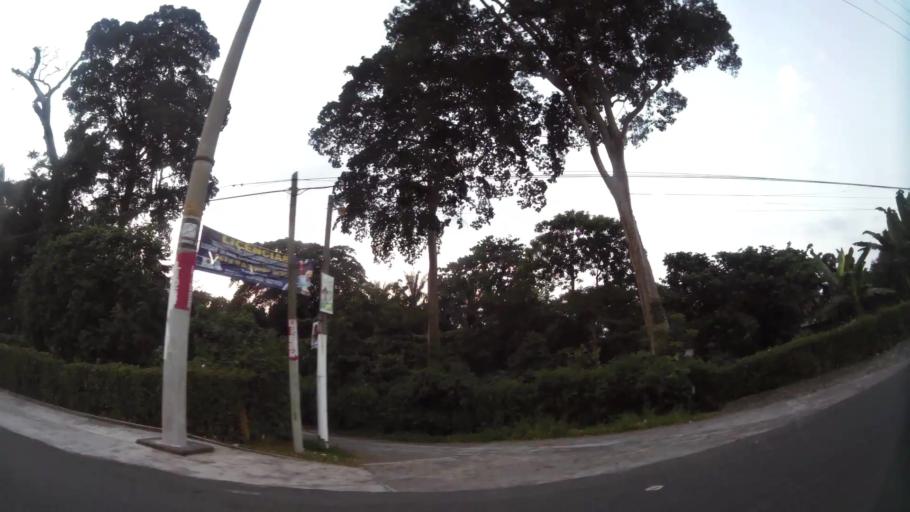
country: GT
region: Retalhuleu
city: San Martin Zapotitlan
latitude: 14.6071
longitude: -91.6079
